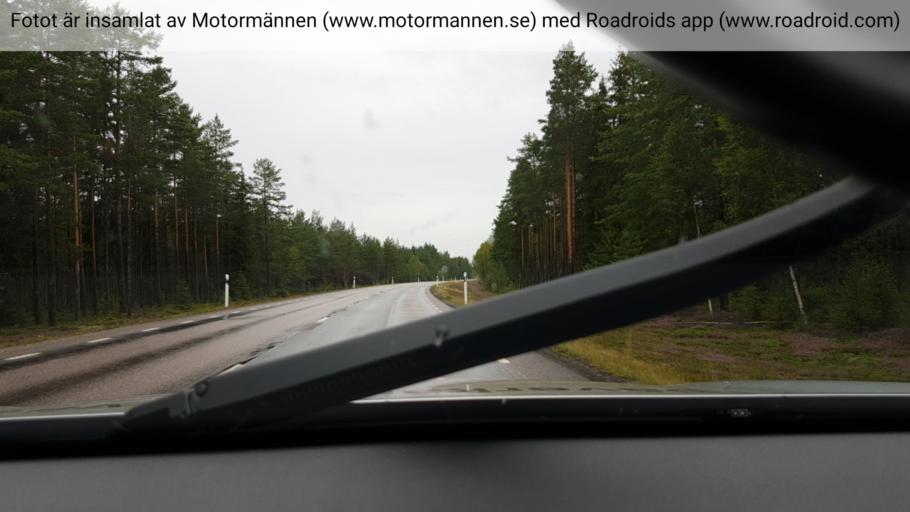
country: SE
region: Gaevleborg
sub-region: Gavle Kommun
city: Hedesunda
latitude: 60.4613
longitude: 16.9450
